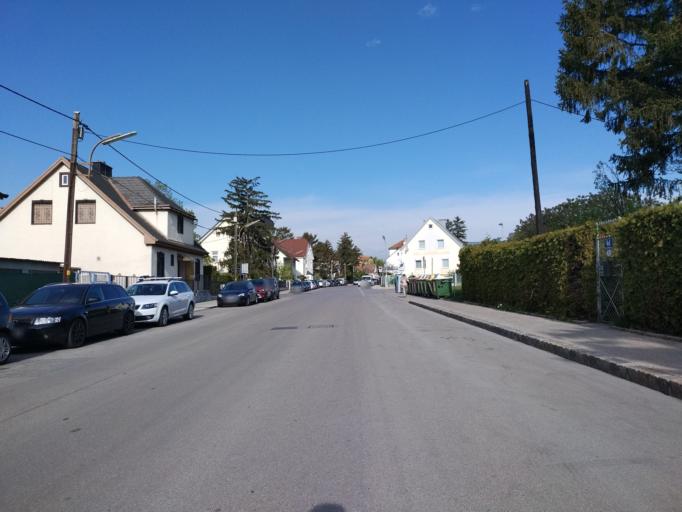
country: AT
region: Lower Austria
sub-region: Politischer Bezirk Modling
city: Vosendorf
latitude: 48.1588
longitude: 16.3122
